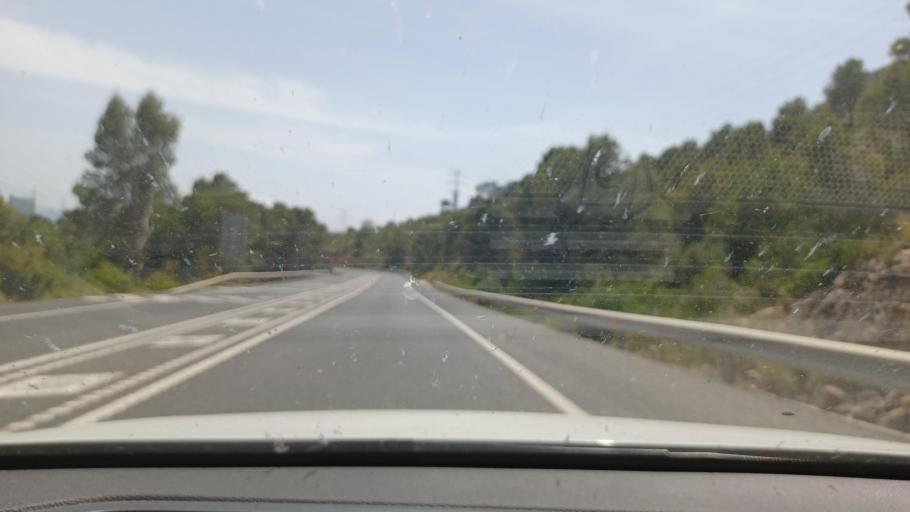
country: ES
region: Catalonia
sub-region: Provincia de Tarragona
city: l'Ametlla de Mar
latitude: 40.9674
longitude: 0.8768
